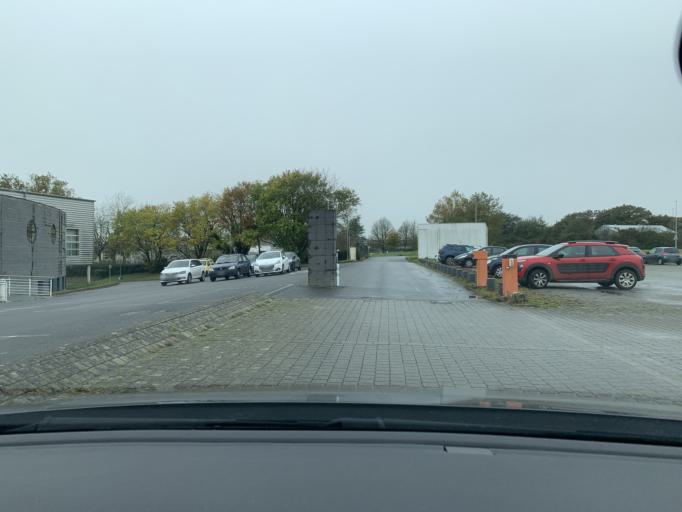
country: FR
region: Brittany
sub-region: Departement du Finistere
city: Roscanvel
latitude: 48.3600
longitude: -4.5670
